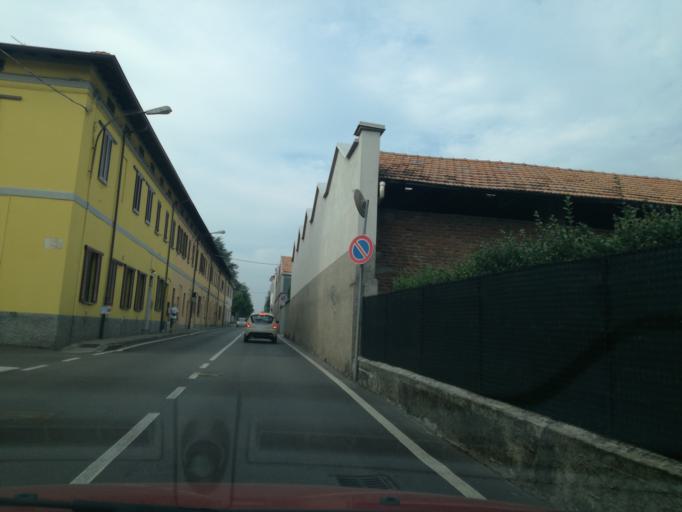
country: IT
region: Lombardy
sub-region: Provincia di Monza e Brianza
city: Vimercate
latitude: 45.6225
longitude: 9.3702
